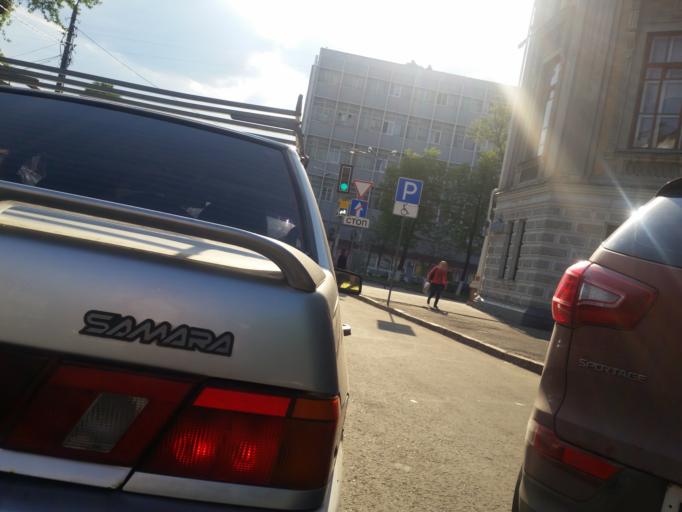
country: RU
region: Ulyanovsk
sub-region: Ulyanovskiy Rayon
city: Ulyanovsk
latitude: 54.3125
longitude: 48.3951
